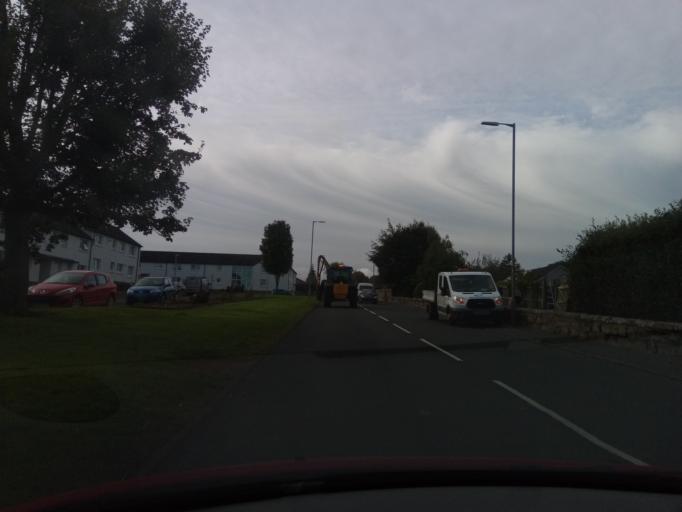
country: GB
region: Scotland
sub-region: The Scottish Borders
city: Kelso
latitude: 55.5939
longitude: -2.4244
